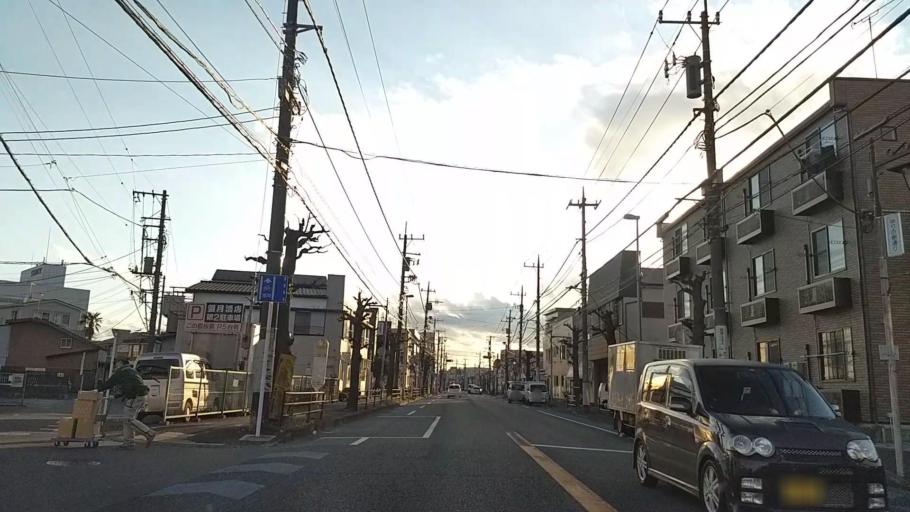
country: JP
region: Kanagawa
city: Atsugi
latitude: 35.4356
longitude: 139.3684
